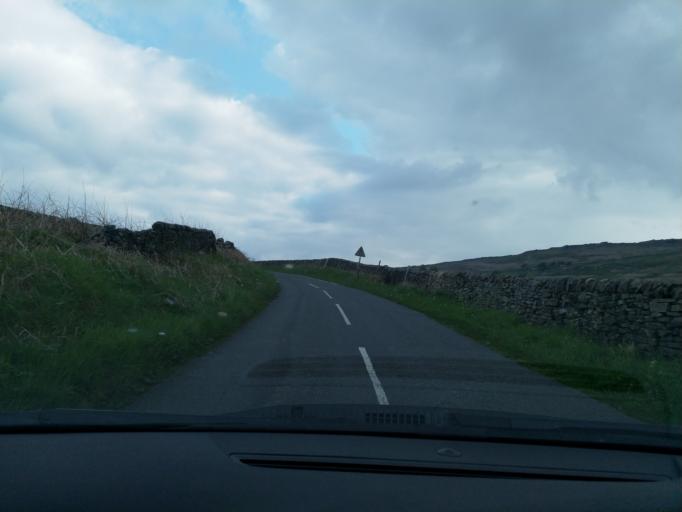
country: GB
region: England
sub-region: Derbyshire
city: Hathersage
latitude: 53.3334
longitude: -1.6299
